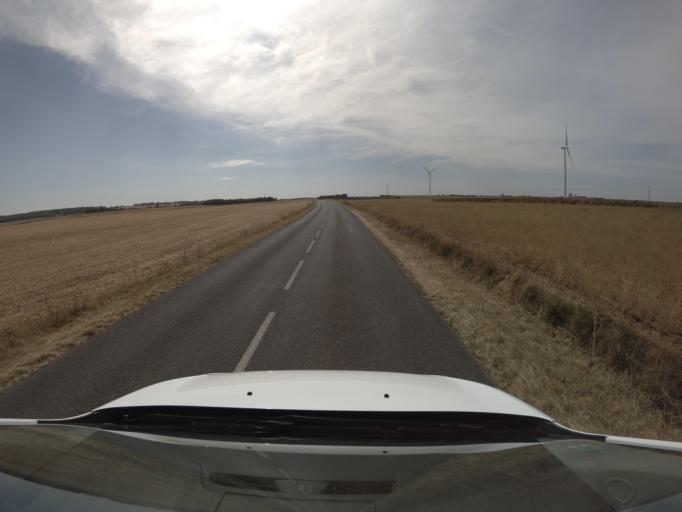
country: FR
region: Poitou-Charentes
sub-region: Departement des Deux-Sevres
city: Saint-Leger-de-Montbrun
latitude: 46.9873
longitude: -0.1626
